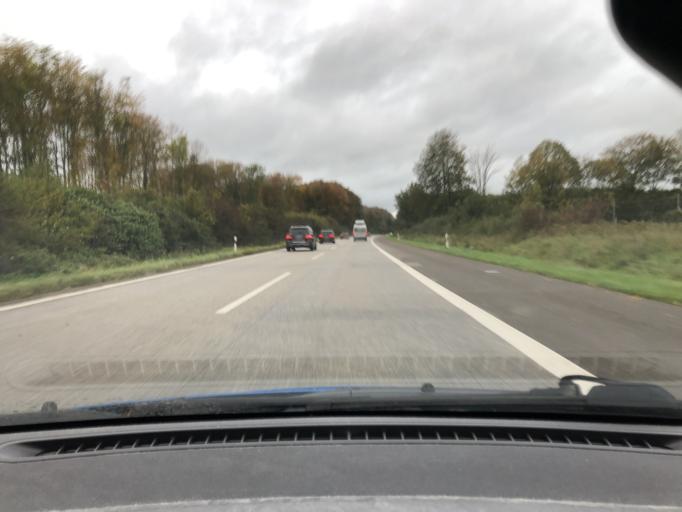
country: DE
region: Schleswig-Holstein
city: Schonbek
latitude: 54.1747
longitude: 9.9584
